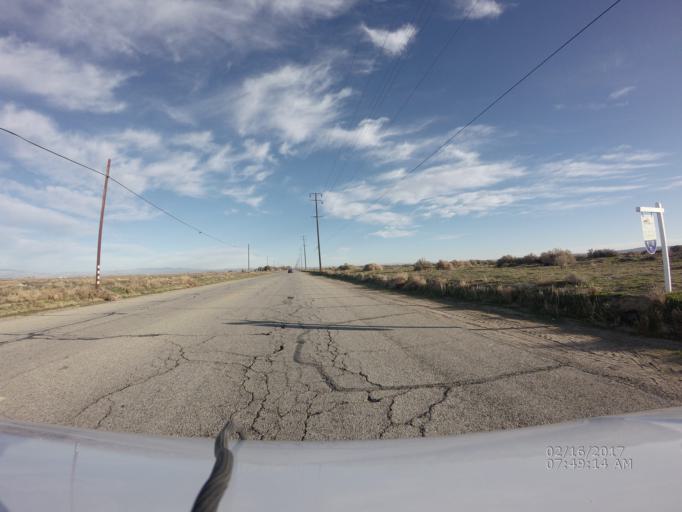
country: US
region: California
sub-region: Los Angeles County
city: Lancaster
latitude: 34.7059
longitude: -117.9697
